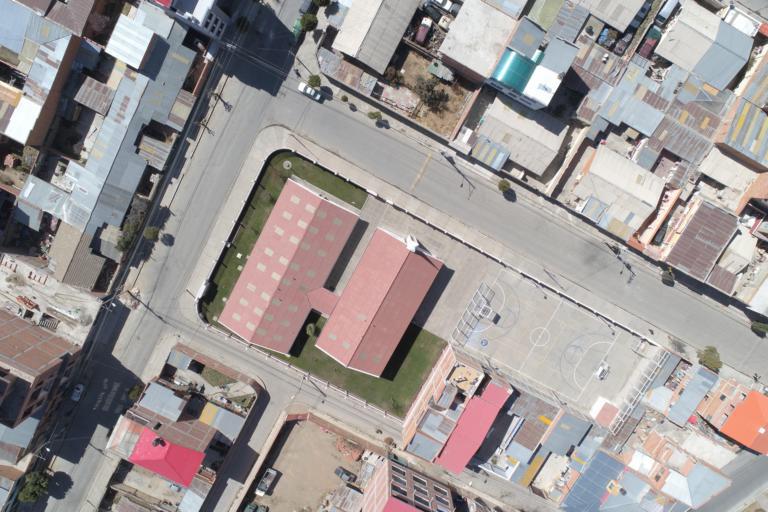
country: BO
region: La Paz
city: La Paz
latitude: -16.5307
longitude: -68.1580
